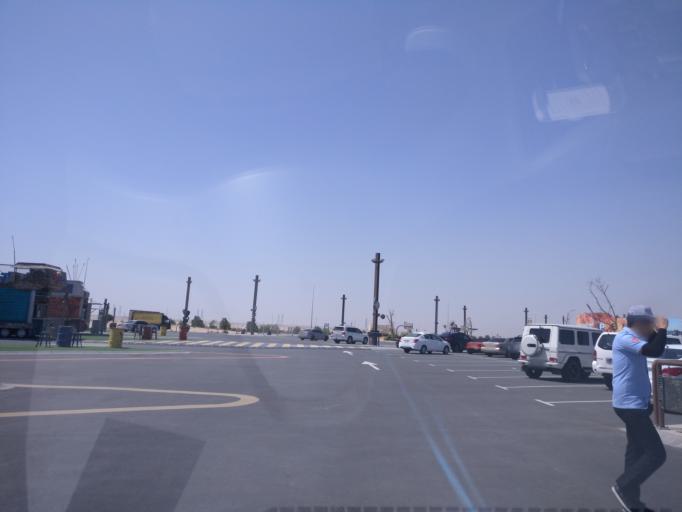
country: AE
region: Dubai
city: Dubai
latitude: 24.9142
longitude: 54.9611
